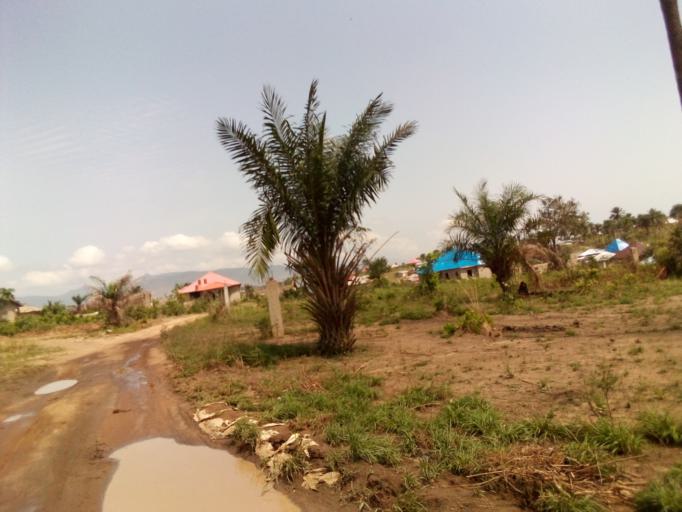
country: SL
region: Western Area
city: Waterloo
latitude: 8.3458
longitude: -13.0179
